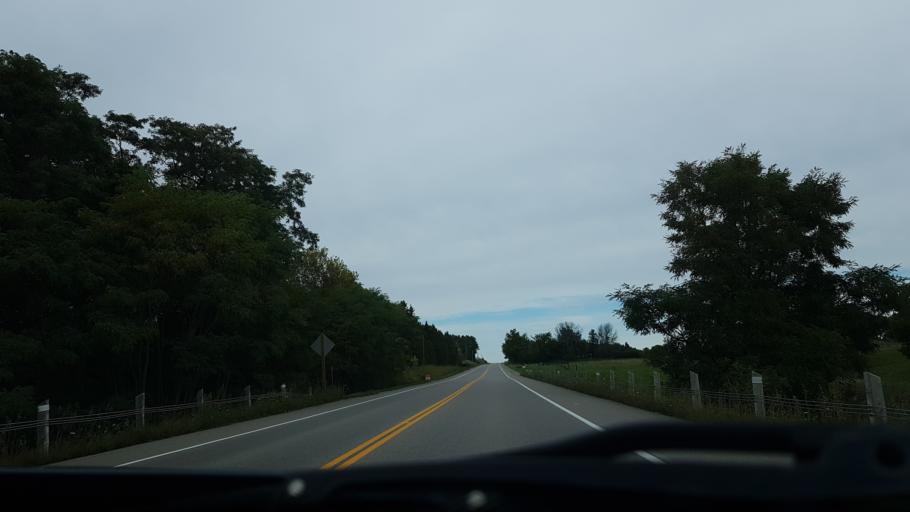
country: CA
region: Ontario
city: Orangeville
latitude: 44.0284
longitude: -80.0058
